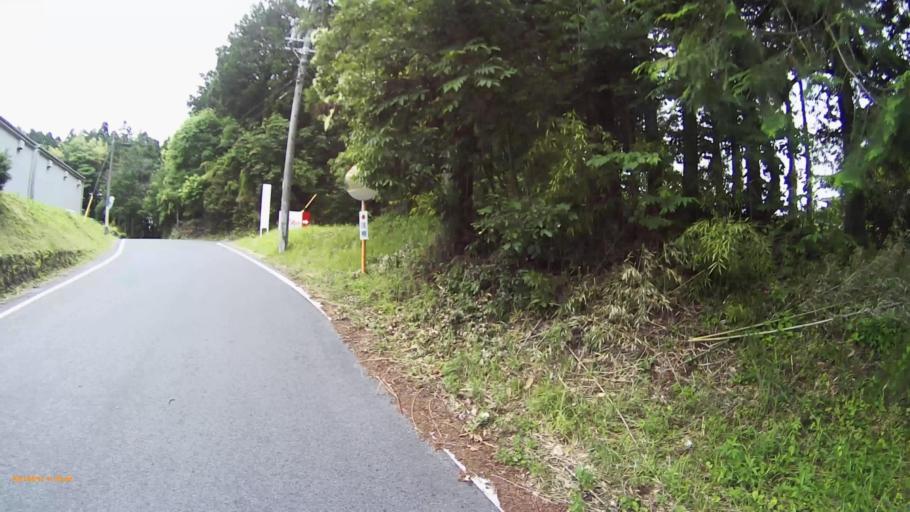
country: JP
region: Gifu
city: Nakatsugawa
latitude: 35.4667
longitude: 137.4334
